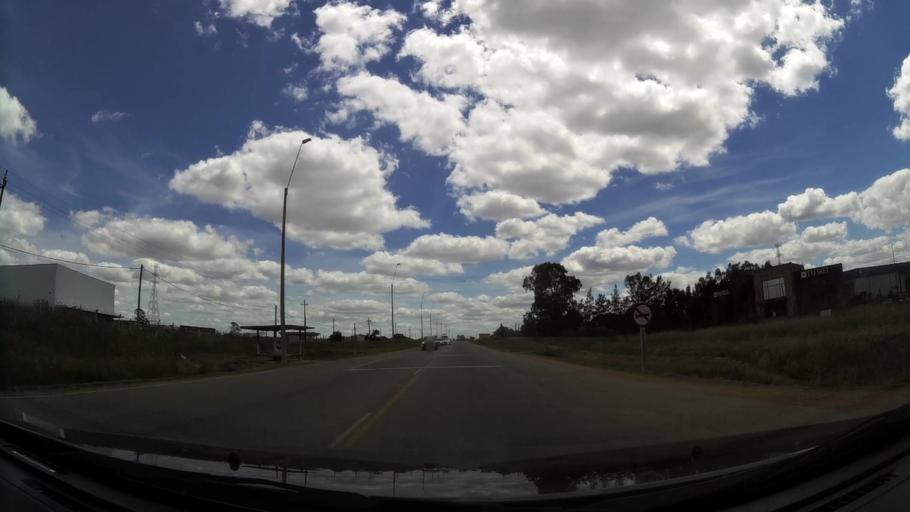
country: UY
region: Canelones
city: Colonia Nicolich
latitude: -34.7976
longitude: -56.0036
